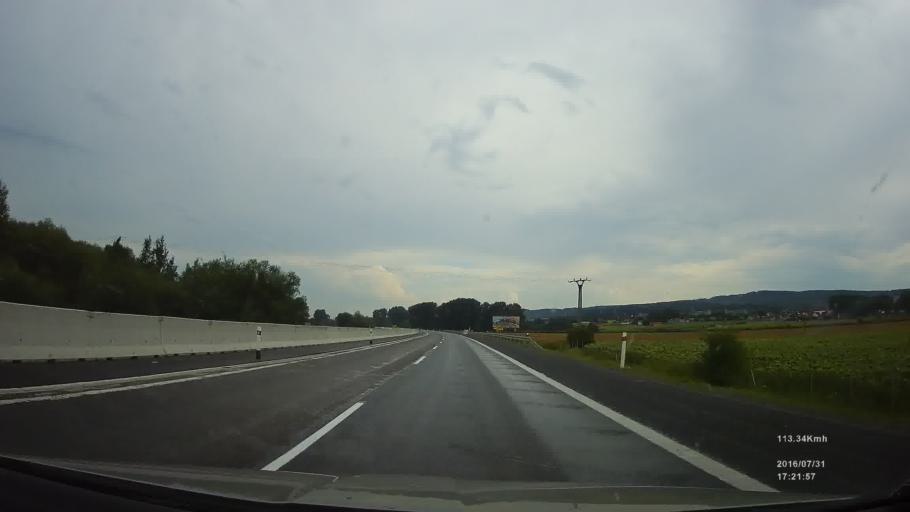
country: SK
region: Kosicky
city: Kosice
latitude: 48.8115
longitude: 21.3093
